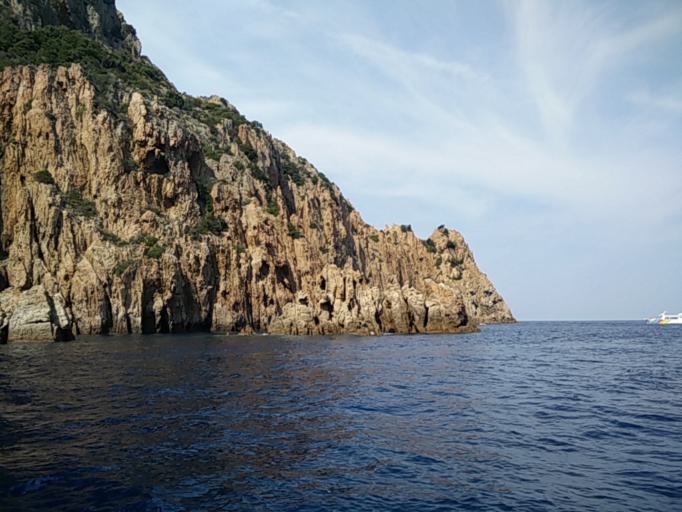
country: FR
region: Corsica
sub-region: Departement de la Corse-du-Sud
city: Cargese
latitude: 42.2389
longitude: 8.5535
